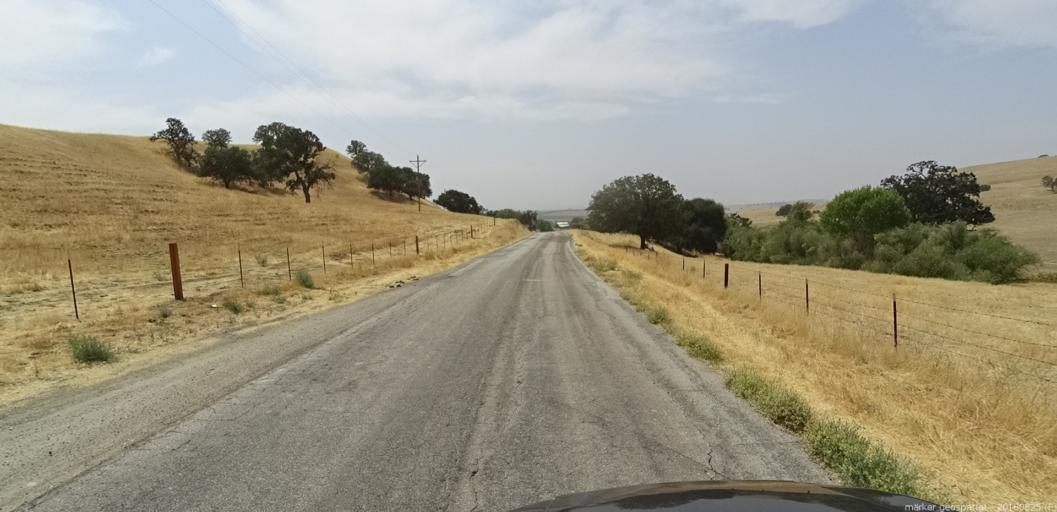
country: US
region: California
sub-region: San Luis Obispo County
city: San Miguel
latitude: 35.7805
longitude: -120.6902
